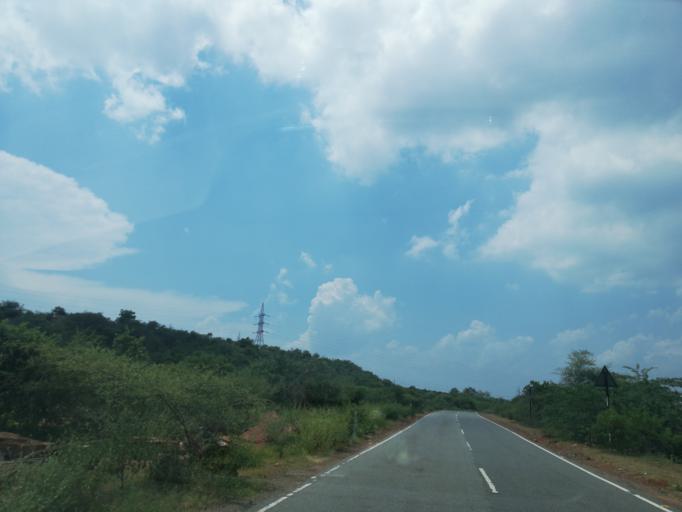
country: IN
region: Andhra Pradesh
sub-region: Guntur
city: Macherla
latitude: 16.5620
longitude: 79.3523
